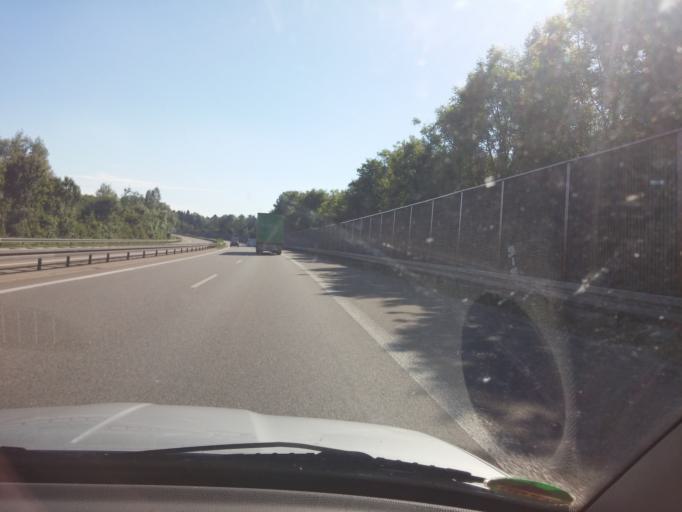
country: DE
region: Baden-Wuerttemberg
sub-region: Tuebingen Region
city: Leutkirch im Allgau
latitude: 47.8647
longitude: 10.0127
